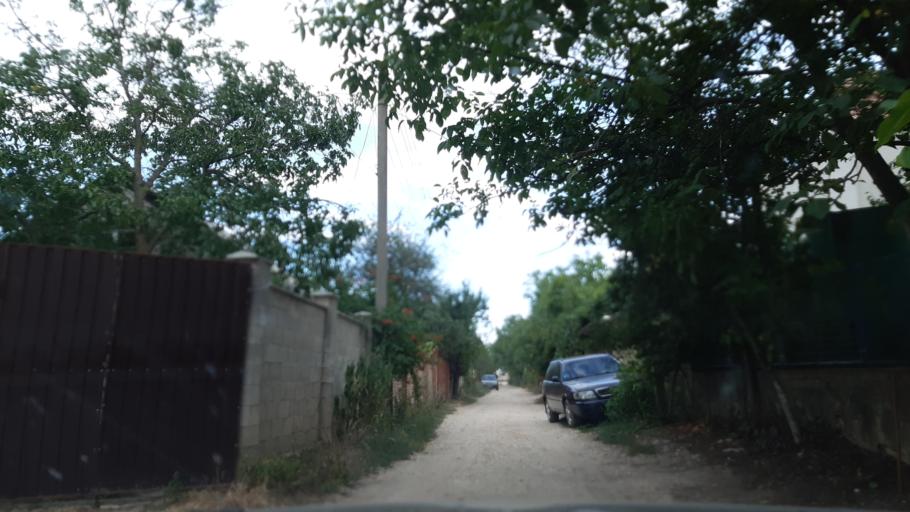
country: MD
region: Chisinau
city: Vatra
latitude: 47.0531
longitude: 28.7295
